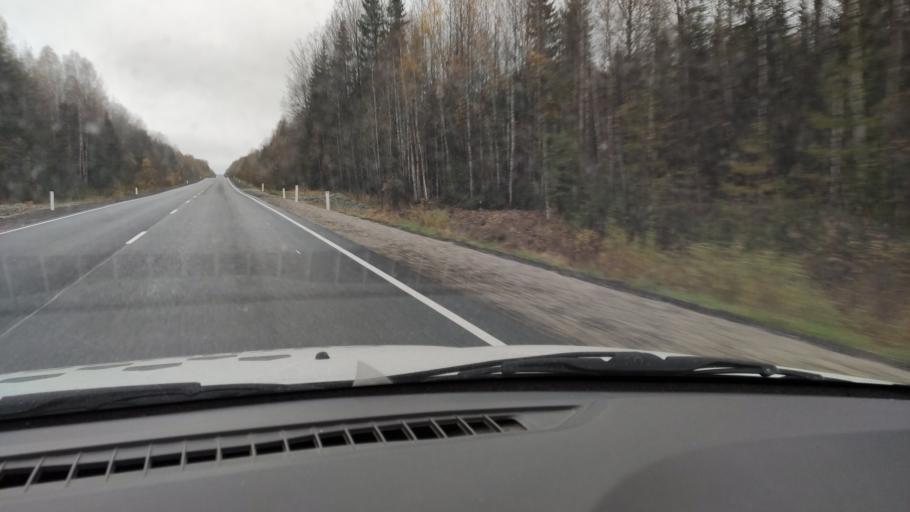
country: RU
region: Kirov
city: Chernaya Kholunitsa
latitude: 58.8792
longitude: 51.4517
